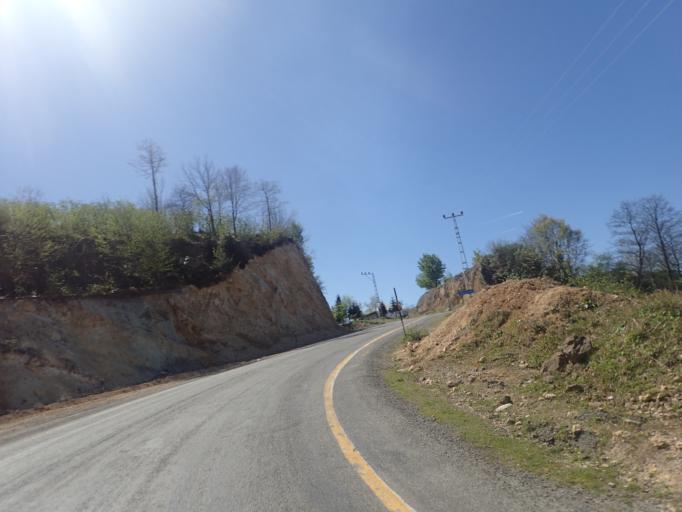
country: TR
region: Ordu
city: Kabaduz
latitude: 40.7991
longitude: 37.9125
